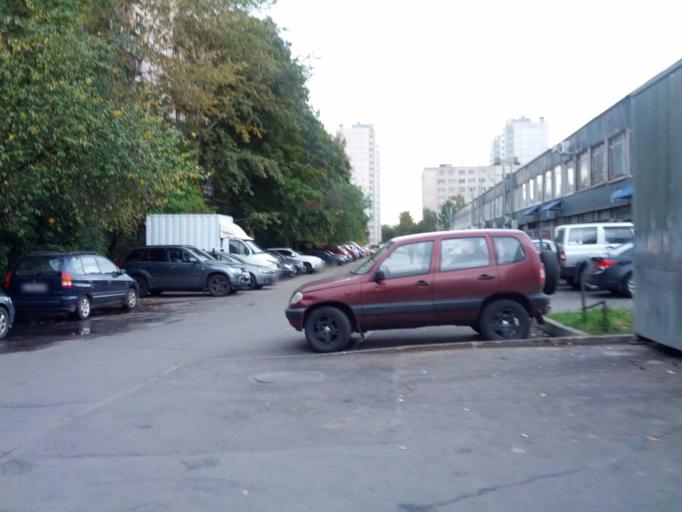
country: RU
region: St.-Petersburg
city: Obukhovo
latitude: 59.8941
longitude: 30.4645
